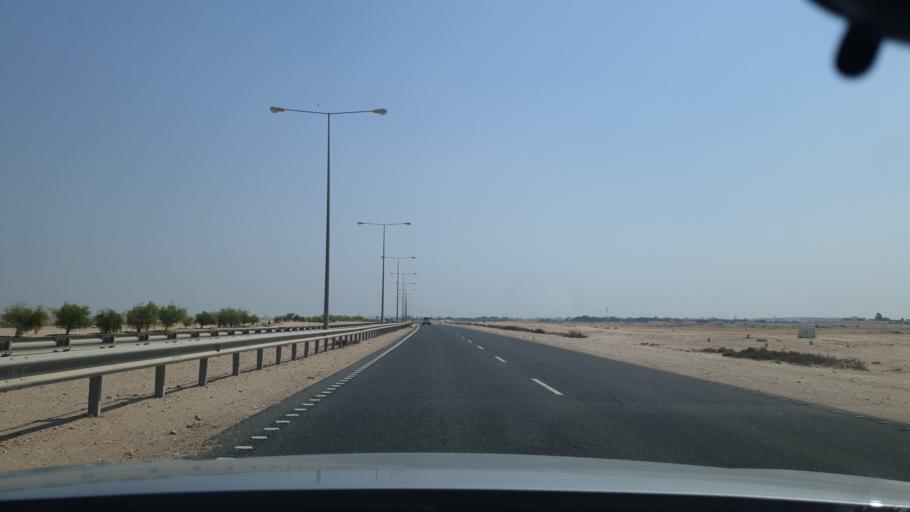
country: QA
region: Al Khawr
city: Al Khawr
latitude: 25.7412
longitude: 51.4864
